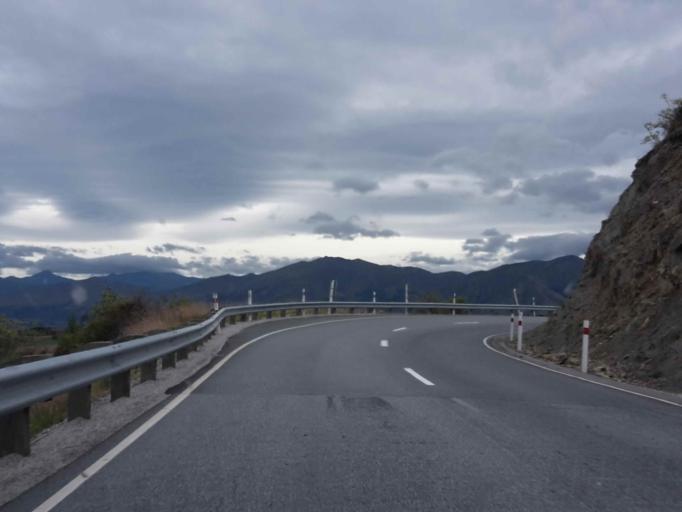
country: NZ
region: Otago
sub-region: Queenstown-Lakes District
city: Arrowtown
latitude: -44.9871
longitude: 168.9034
